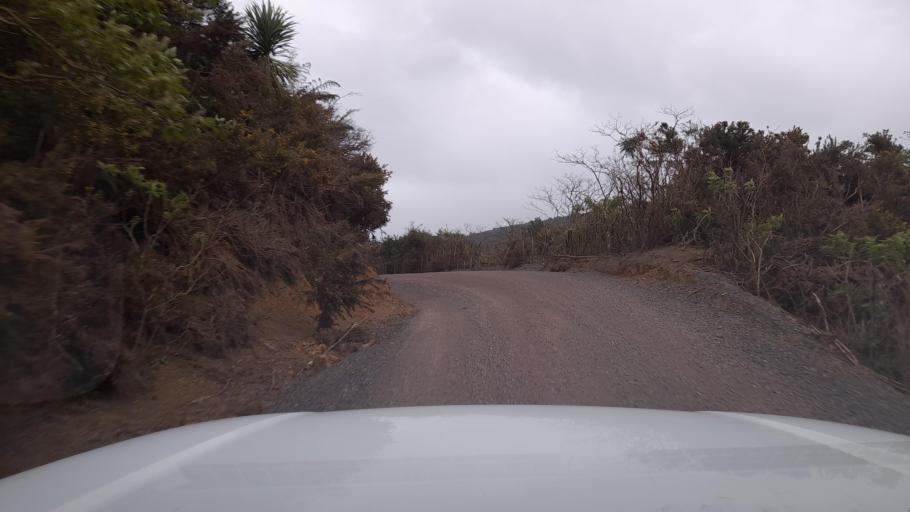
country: NZ
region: Northland
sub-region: Far North District
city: Paihia
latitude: -35.3479
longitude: 174.2253
